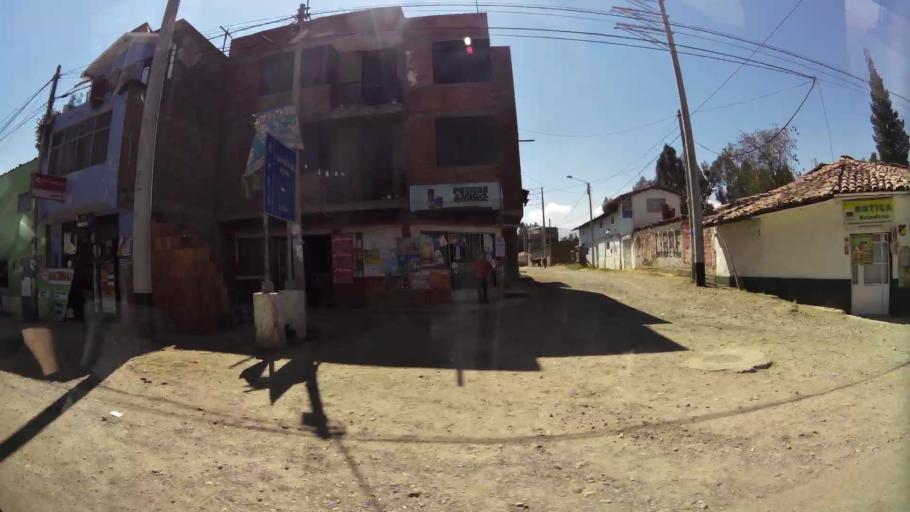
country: PE
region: Junin
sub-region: Provincia de Concepcion
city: Matahuasi
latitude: -11.8913
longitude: -75.3431
